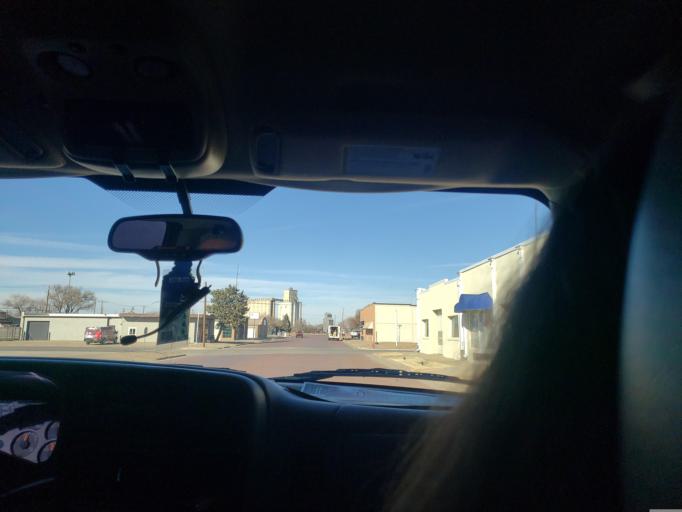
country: US
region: Texas
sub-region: Dallam County
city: Dalhart
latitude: 36.0612
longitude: -102.5243
